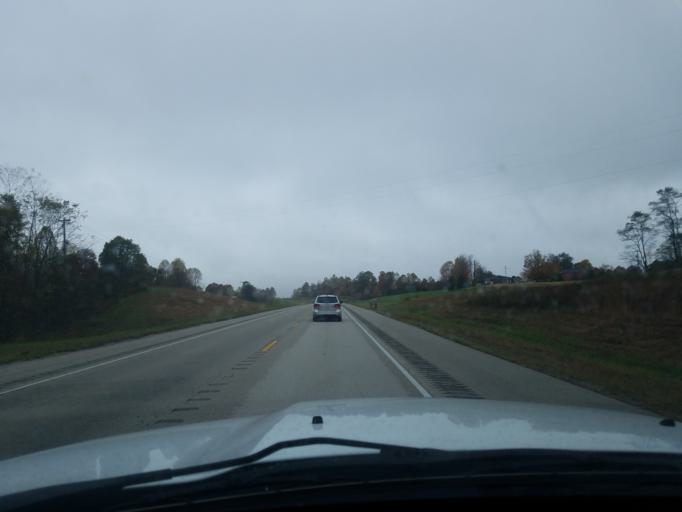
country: US
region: Kentucky
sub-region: Larue County
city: Hodgenville
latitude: 37.4628
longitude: -85.5666
